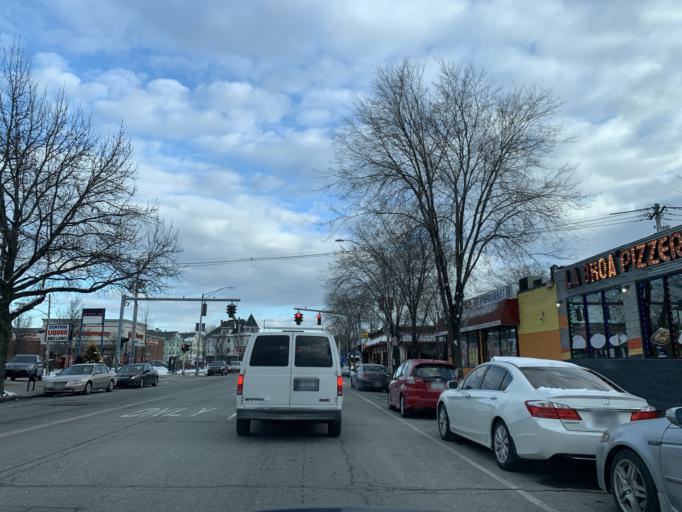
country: US
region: Rhode Island
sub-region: Providence County
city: Providence
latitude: 41.7992
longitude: -71.4159
